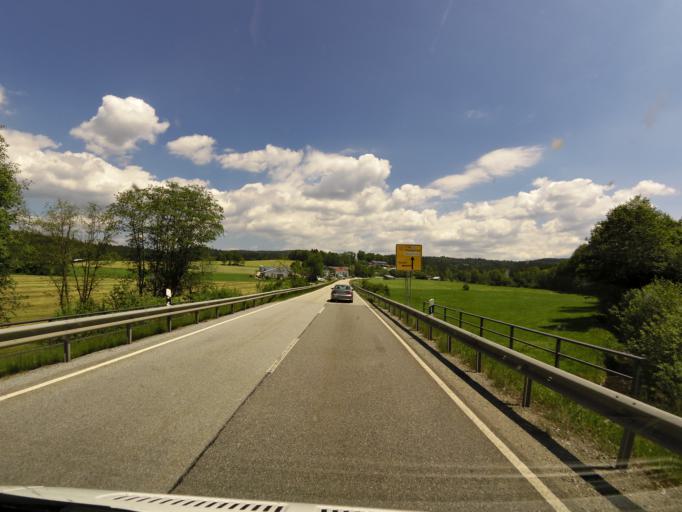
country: DE
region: Bavaria
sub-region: Lower Bavaria
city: Hinterschmiding
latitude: 48.8377
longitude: 13.5960
